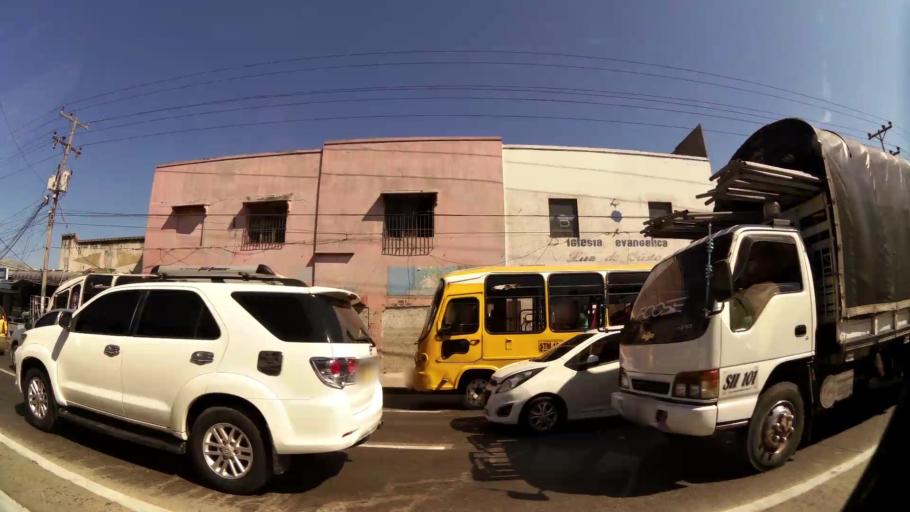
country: CO
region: Atlantico
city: Barranquilla
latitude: 10.9659
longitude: -74.7820
